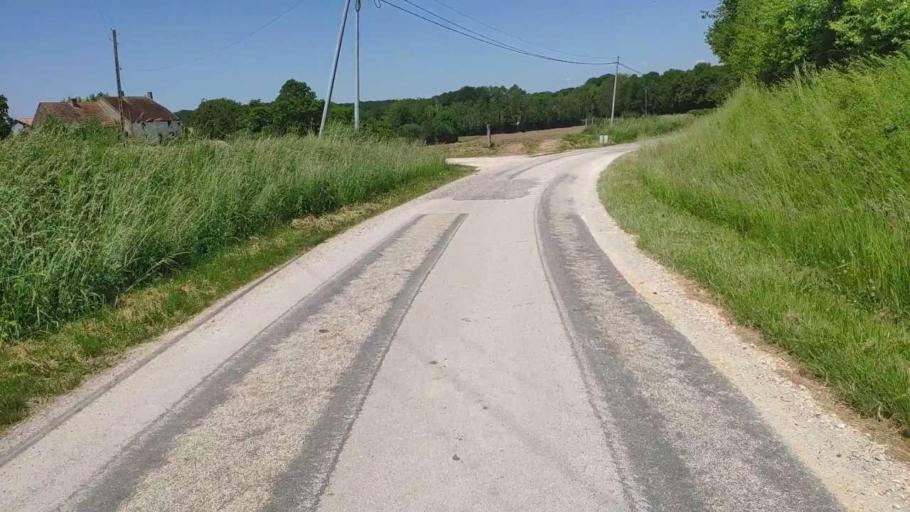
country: FR
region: Franche-Comte
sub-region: Departement du Jura
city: Bletterans
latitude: 46.7569
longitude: 5.4215
